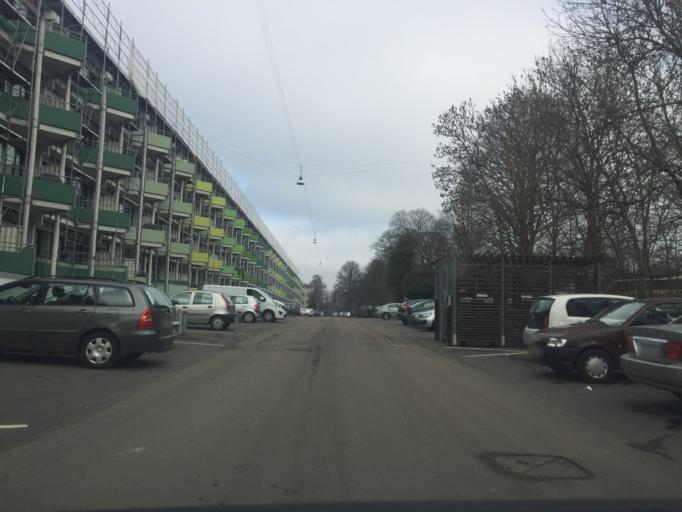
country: DK
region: Capital Region
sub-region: Gentofte Kommune
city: Charlottenlund
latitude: 55.7226
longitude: 12.5633
